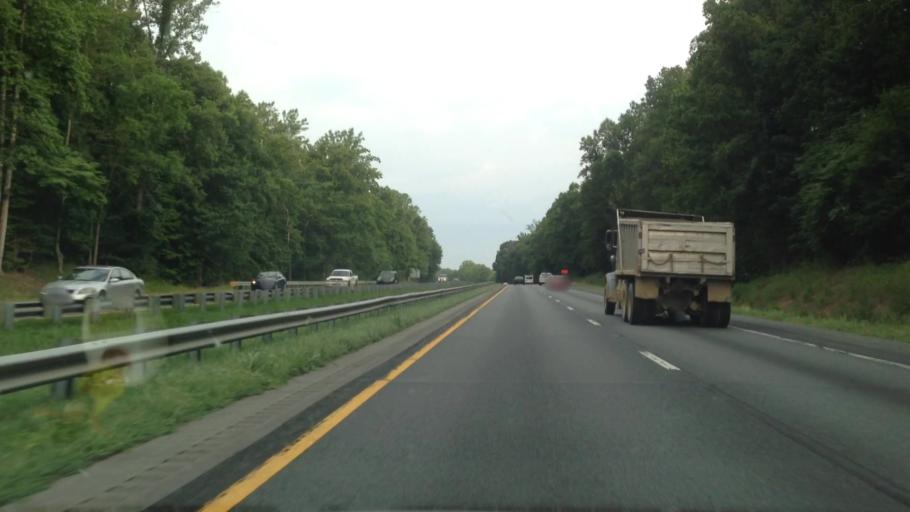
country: US
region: North Carolina
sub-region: Forsyth County
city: Rural Hall
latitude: 36.2178
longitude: -80.3096
